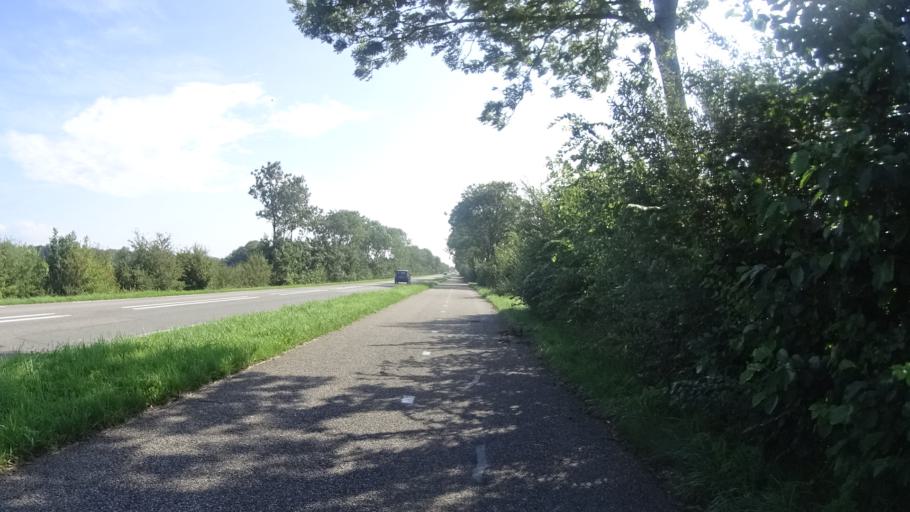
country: NL
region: Friesland
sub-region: Menameradiel
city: Dronryp
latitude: 53.1952
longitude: 5.6132
